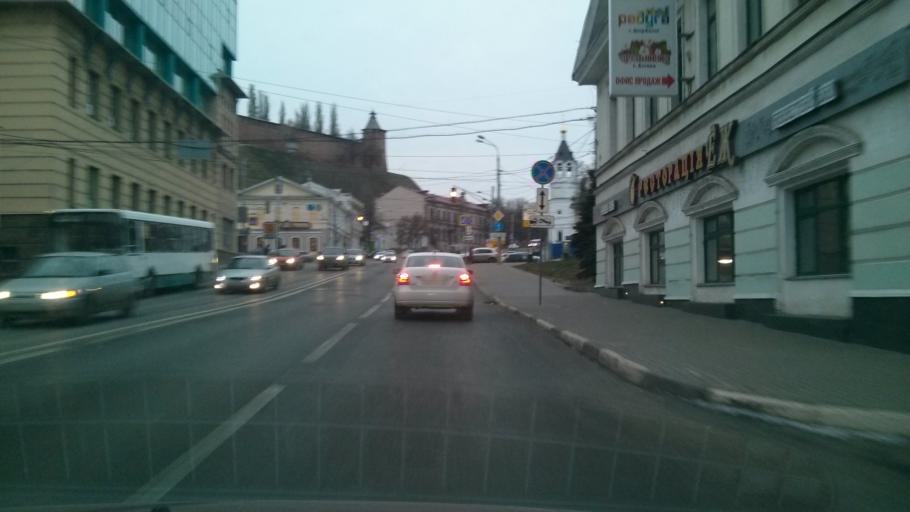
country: RU
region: Nizjnij Novgorod
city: Nizhniy Novgorod
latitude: 56.3306
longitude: 43.9956
